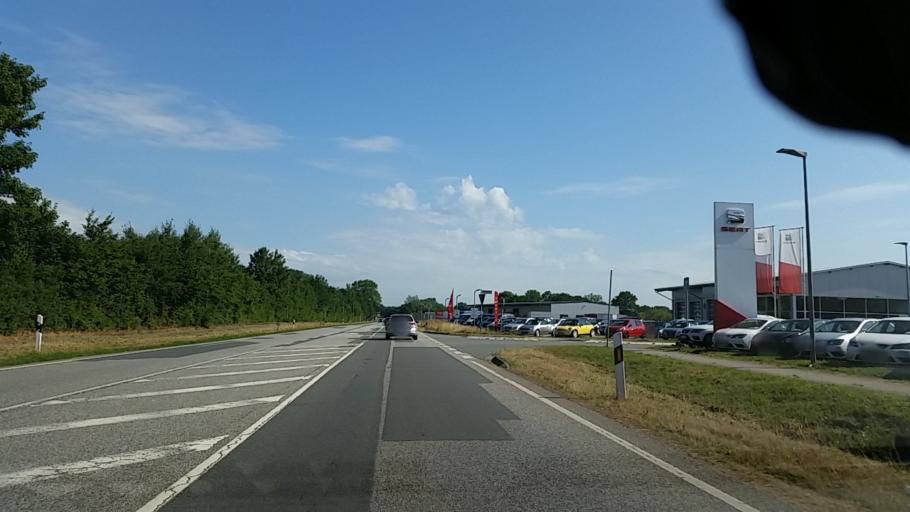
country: DE
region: Schleswig-Holstein
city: Kaltenkirchen
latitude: 53.8183
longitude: 9.9706
